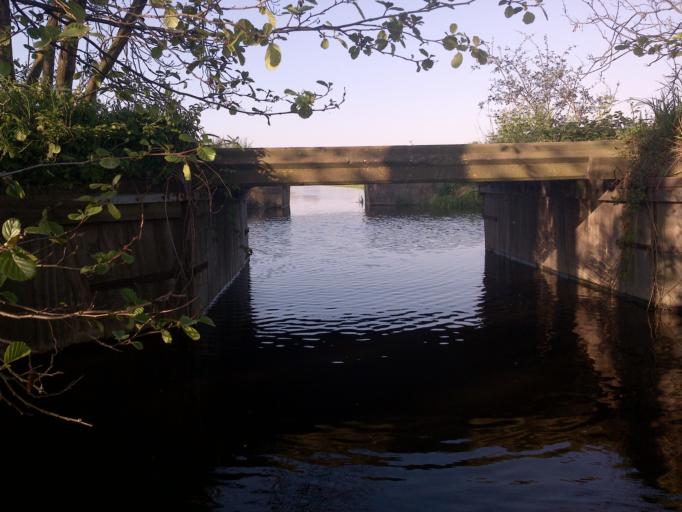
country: NL
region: South Holland
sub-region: Gemeente Voorschoten
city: Voorschoten
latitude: 52.1216
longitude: 4.4253
